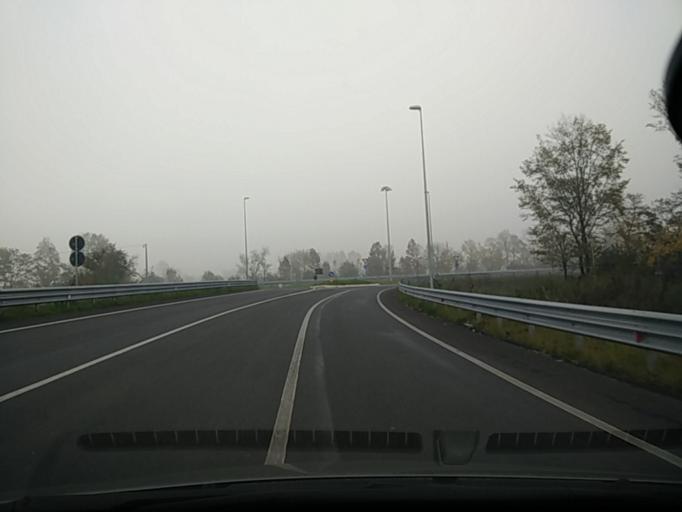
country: IT
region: Veneto
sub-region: Provincia di Venezia
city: Robegano
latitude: 45.5628
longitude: 12.1343
